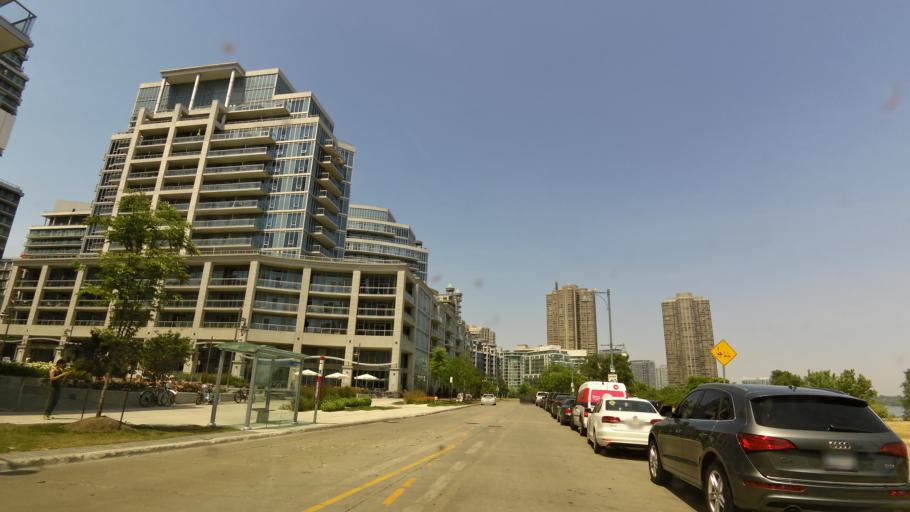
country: CA
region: Ontario
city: Etobicoke
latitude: 43.6265
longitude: -79.4769
